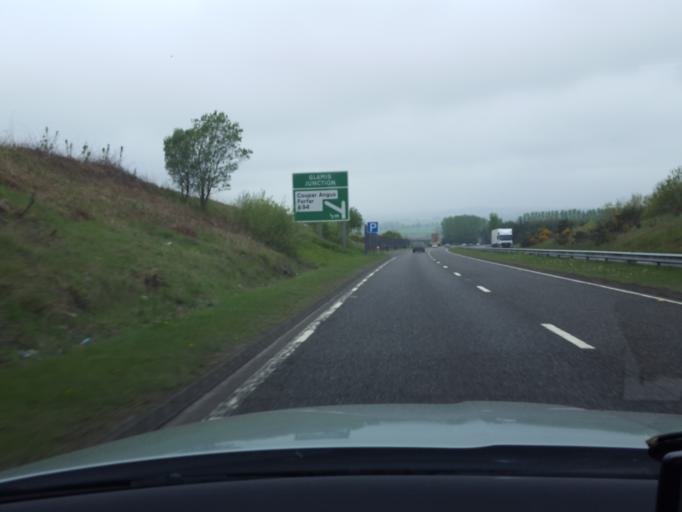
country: GB
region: Scotland
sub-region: Angus
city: Forfar
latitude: 56.6281
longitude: -2.9189
